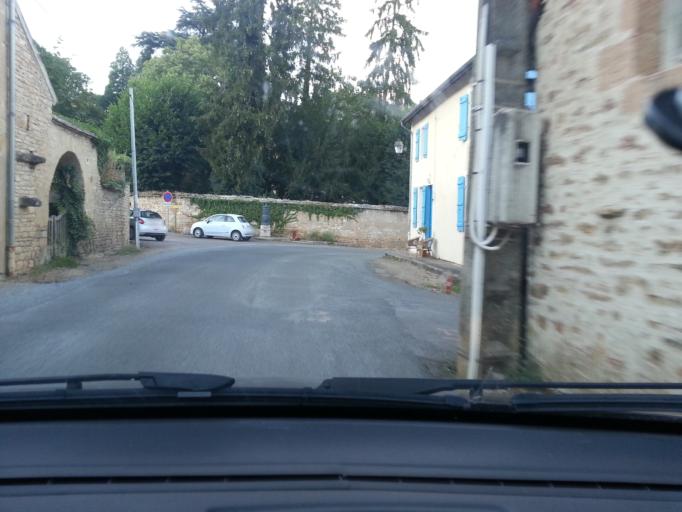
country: FR
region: Bourgogne
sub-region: Departement de Saone-et-Loire
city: Givry
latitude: 46.7790
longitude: 4.7293
